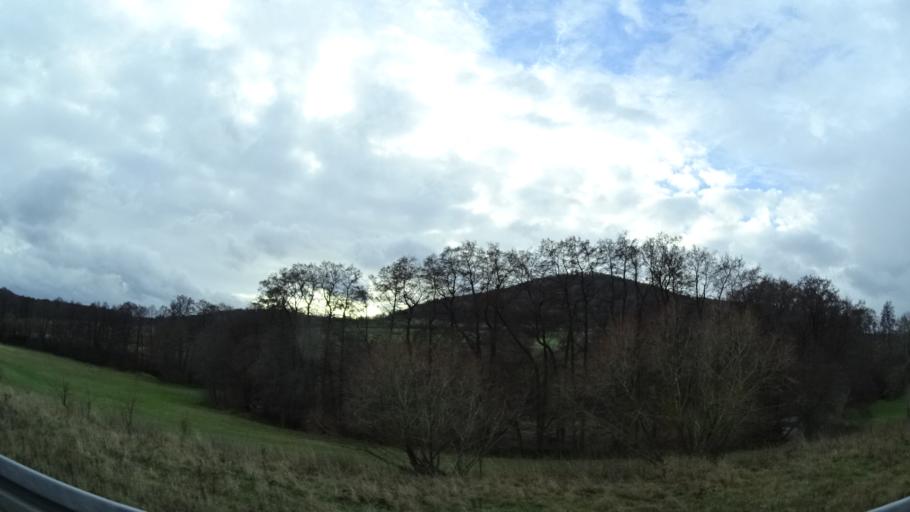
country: DE
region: Thuringia
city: Oberkatz
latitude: 50.5629
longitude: 10.2484
